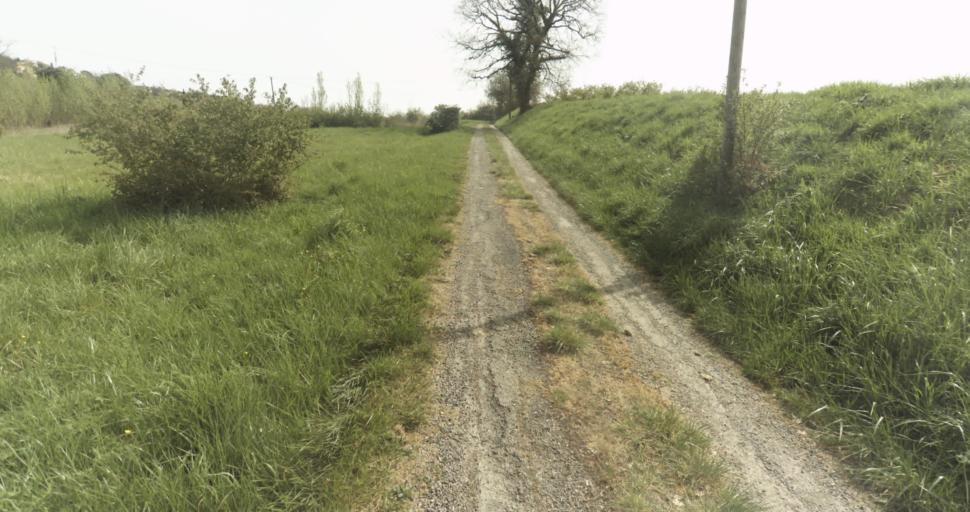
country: FR
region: Midi-Pyrenees
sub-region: Departement du Tarn-et-Garonne
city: Moissac
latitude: 44.1074
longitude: 1.0637
